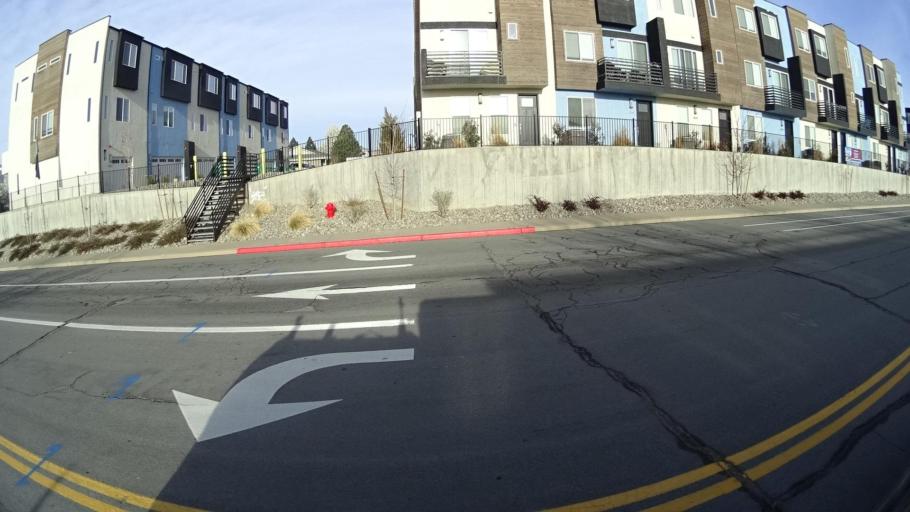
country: US
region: Nevada
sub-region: Washoe County
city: Reno
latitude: 39.5210
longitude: -119.8587
